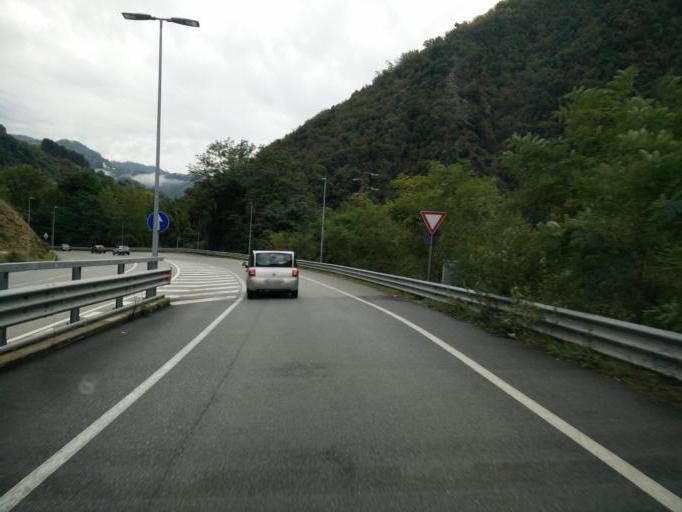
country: IT
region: Tuscany
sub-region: Provincia di Lucca
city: Valdottavo
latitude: 43.9294
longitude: 10.5080
